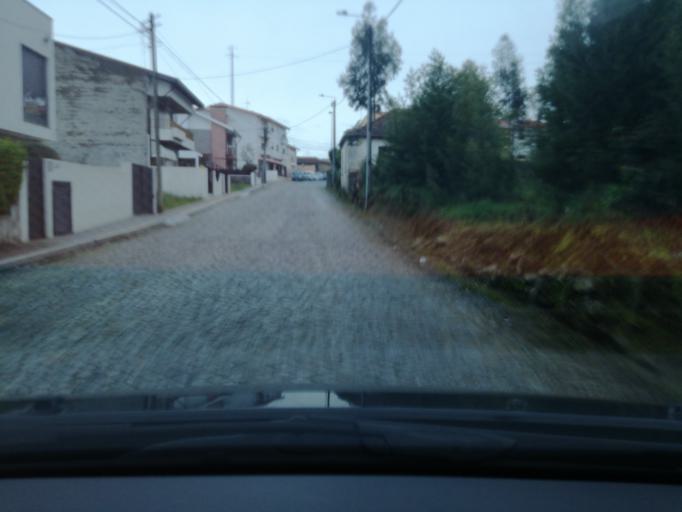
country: PT
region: Porto
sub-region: Maia
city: Anta
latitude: 41.2651
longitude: -8.6367
